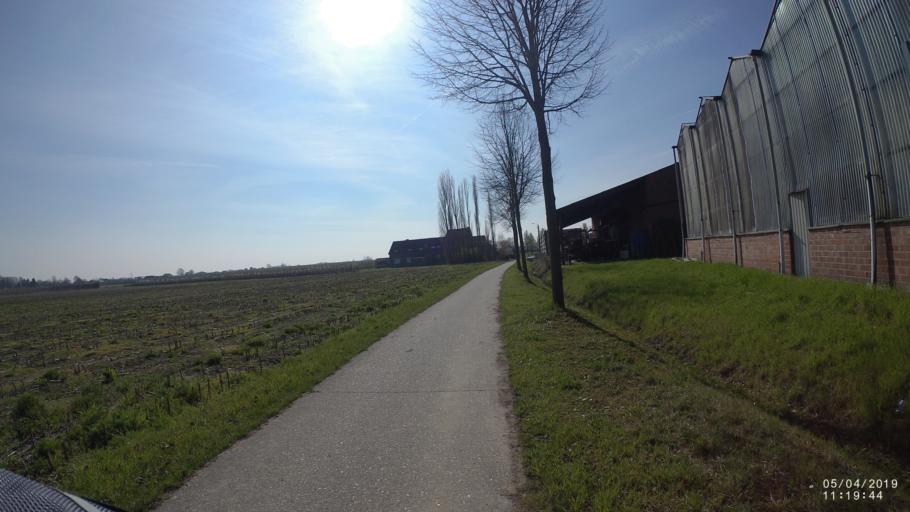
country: BE
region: Flanders
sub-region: Provincie Limburg
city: Herk-de-Stad
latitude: 50.9235
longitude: 5.1750
